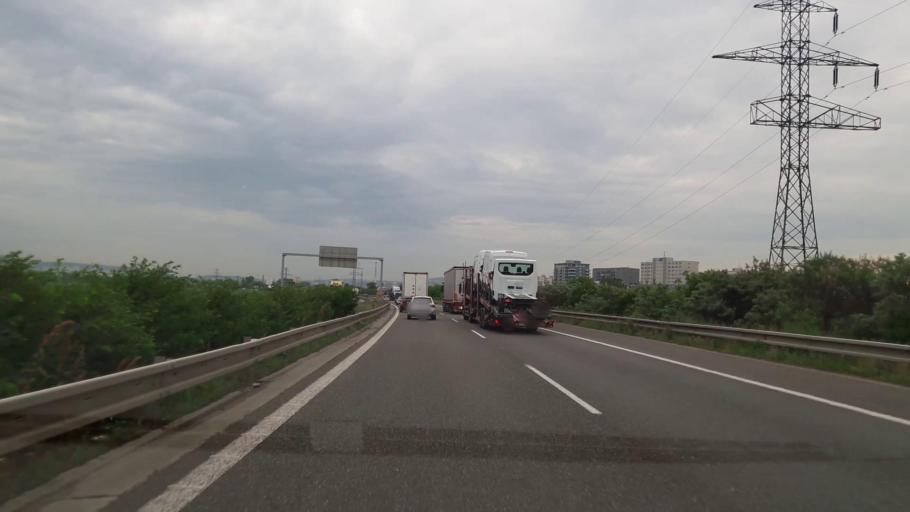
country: AT
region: Burgenland
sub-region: Politischer Bezirk Neusiedl am See
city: Kittsee
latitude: 48.0954
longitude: 17.0987
